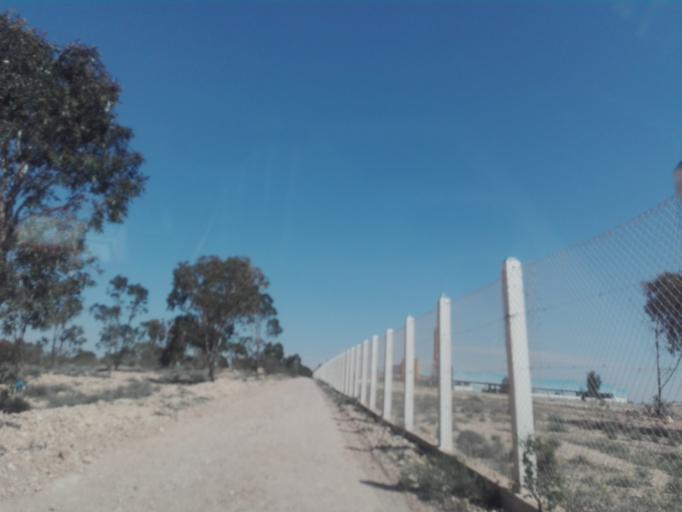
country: TN
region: Safaqis
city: Sfax
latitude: 34.7031
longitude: 10.5274
